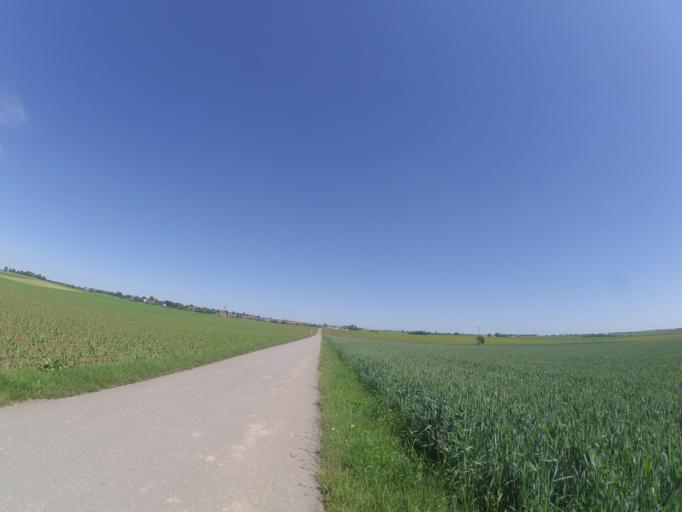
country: DE
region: Baden-Wuerttemberg
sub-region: Tuebingen Region
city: Dornstadt
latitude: 48.4713
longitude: 9.9164
